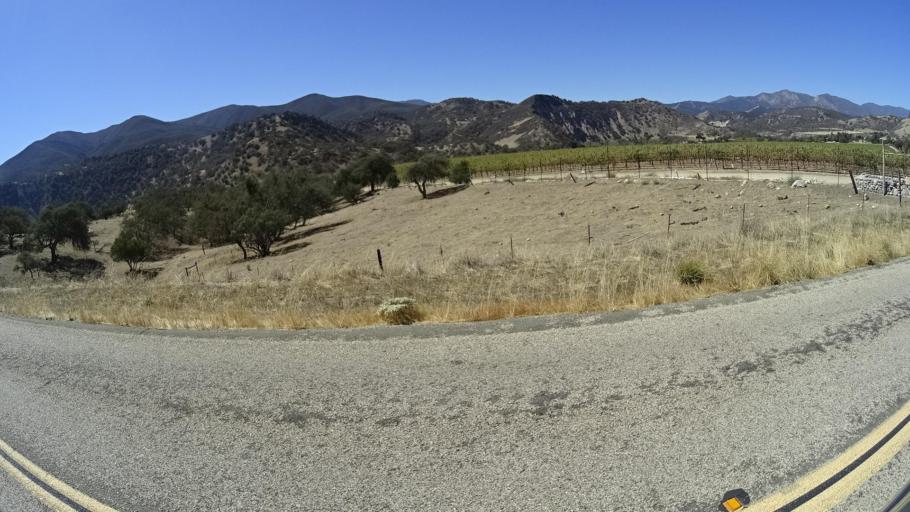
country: US
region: California
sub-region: Monterey County
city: Greenfield
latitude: 36.2692
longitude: -121.3796
